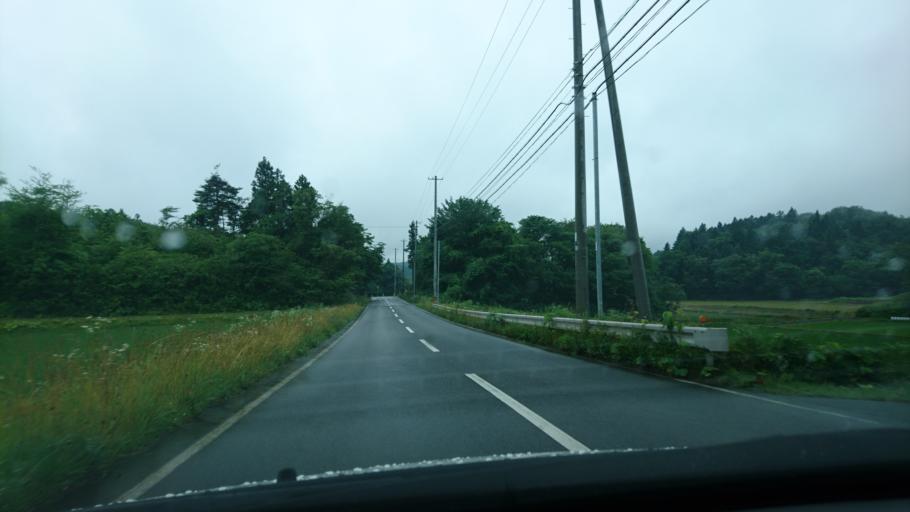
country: JP
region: Iwate
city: Ichinoseki
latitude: 38.9311
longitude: 141.0292
